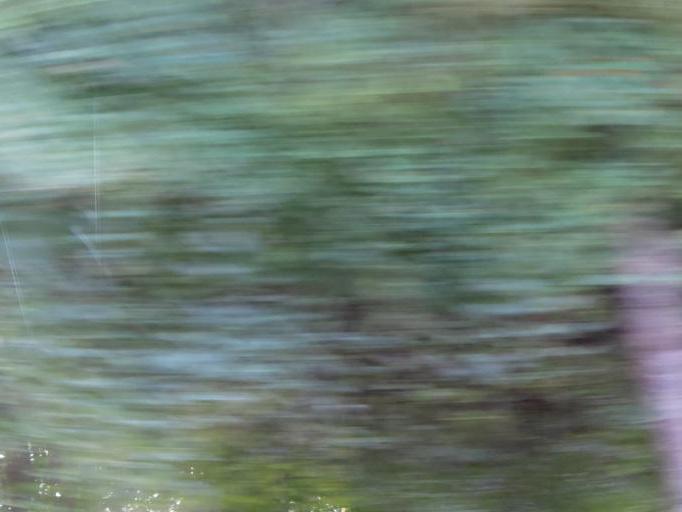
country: US
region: Tennessee
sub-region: Union County
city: Luttrell
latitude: 36.2226
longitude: -83.7416
